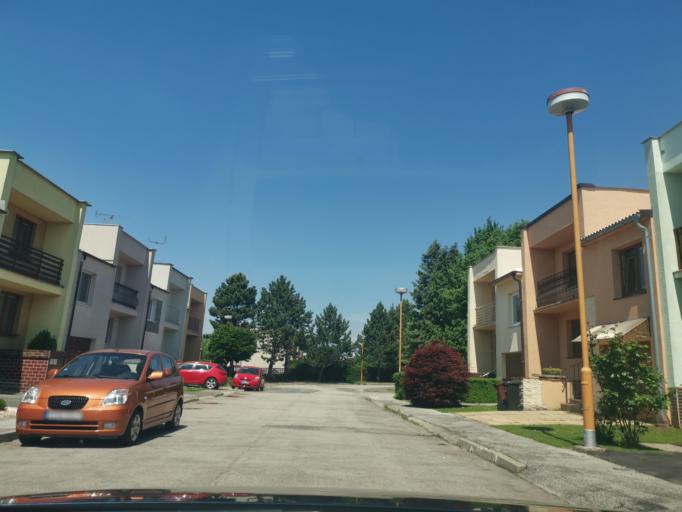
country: SK
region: Trnavsky
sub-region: Okres Senica
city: Senica
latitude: 48.6710
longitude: 17.3655
